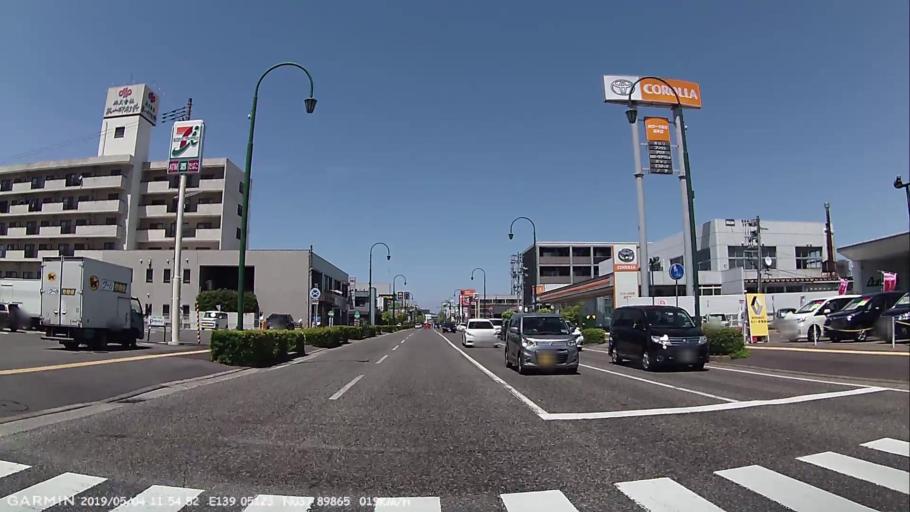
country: JP
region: Niigata
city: Niigata-shi
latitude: 37.8987
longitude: 139.0512
